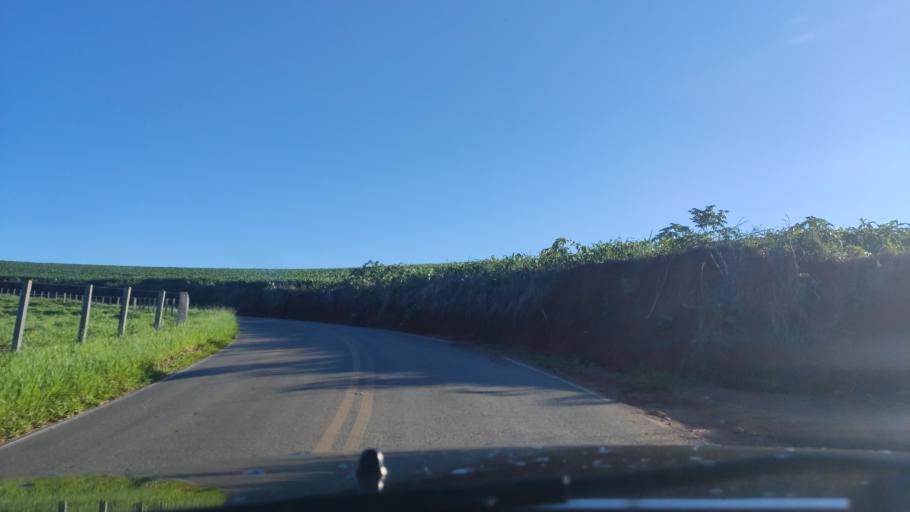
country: BR
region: Sao Paulo
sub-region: Aguas De Lindoia
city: Aguas de Lindoia
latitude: -22.5644
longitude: -46.6213
